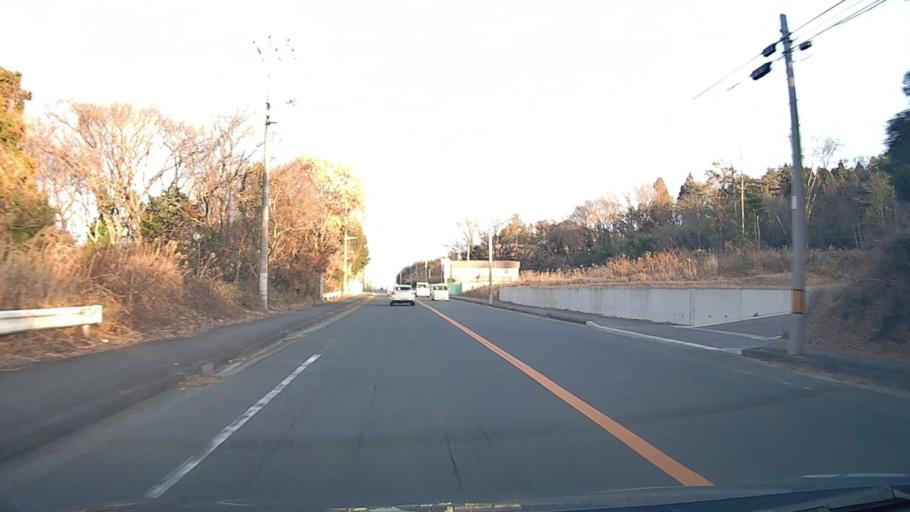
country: JP
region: Ibaraki
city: Kitaibaraki
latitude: 36.8053
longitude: 140.7485
